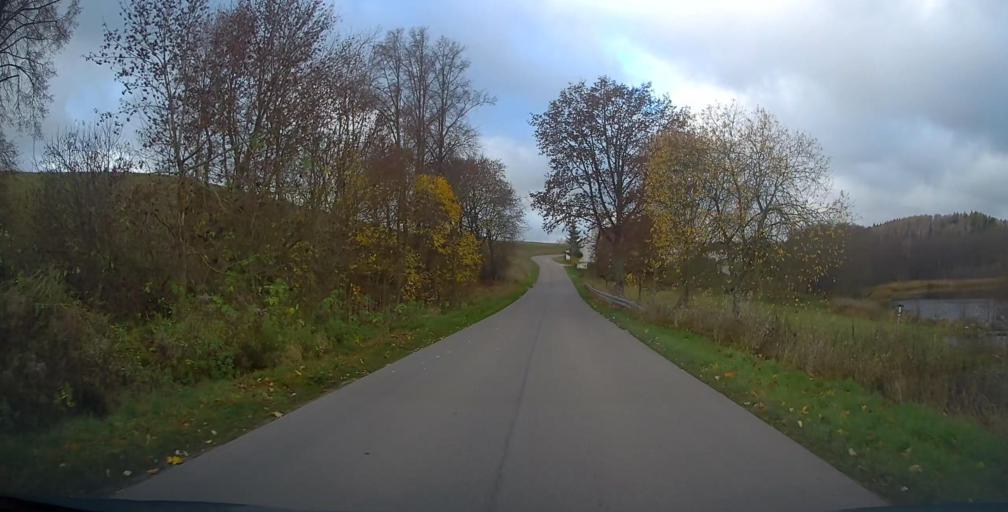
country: PL
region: Podlasie
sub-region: Suwalki
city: Suwalki
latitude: 54.2707
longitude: 22.9189
